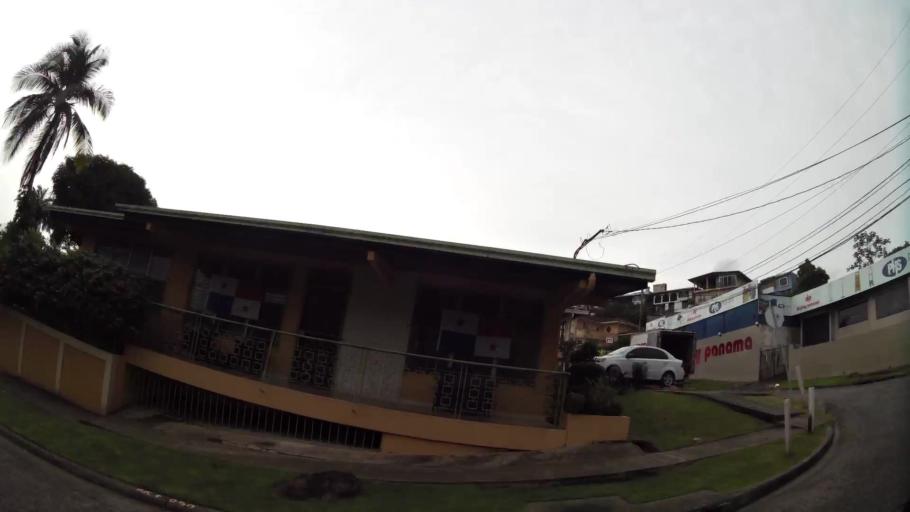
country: PA
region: Panama
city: Panama
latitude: 9.0144
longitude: -79.5256
